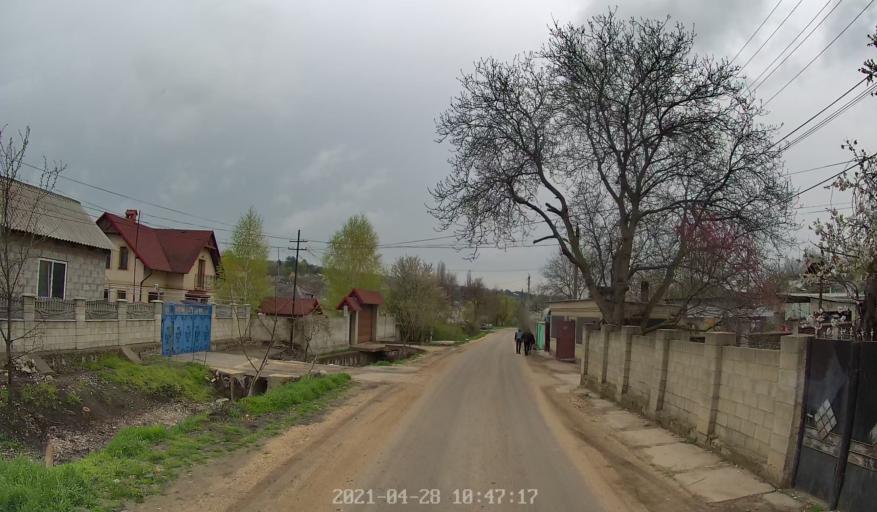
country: MD
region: Chisinau
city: Singera
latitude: 46.9899
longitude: 28.9481
